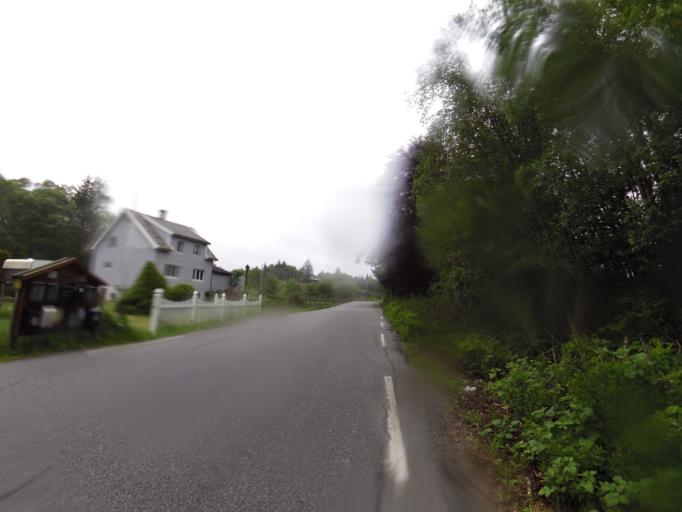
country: NO
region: Hordaland
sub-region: Sveio
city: Sveio
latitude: 59.5256
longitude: 5.2807
